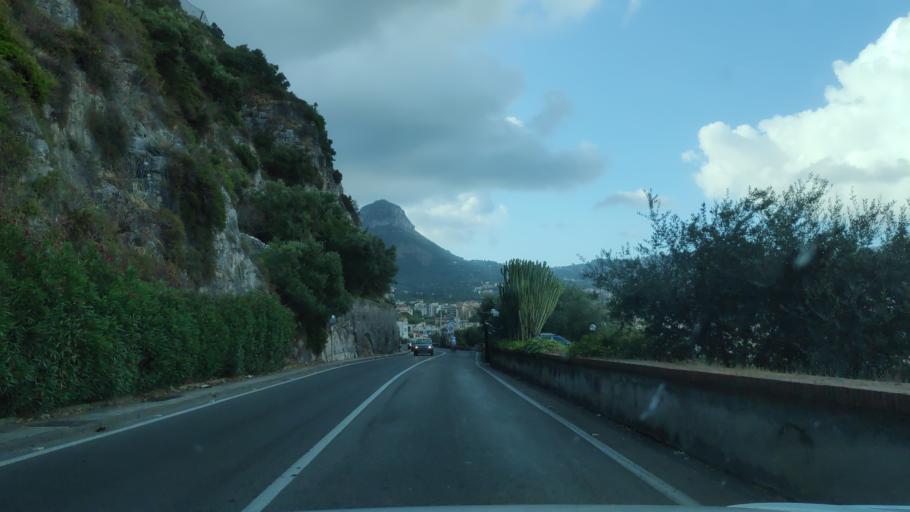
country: IT
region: Campania
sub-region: Provincia di Napoli
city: Meta
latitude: 40.6464
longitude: 14.4133
